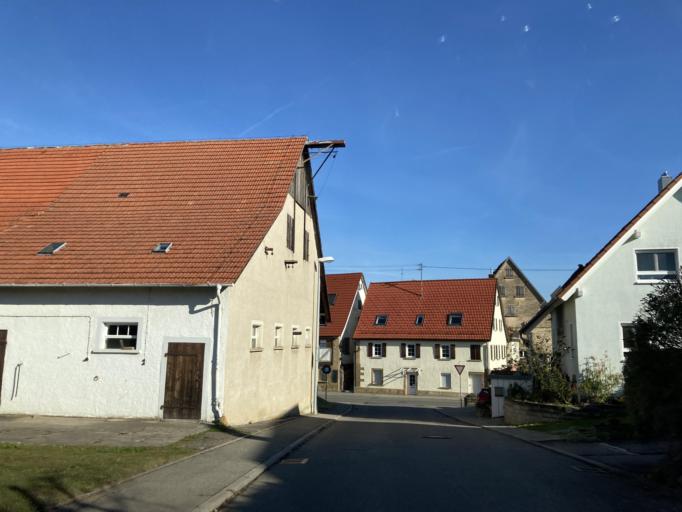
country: DE
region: Baden-Wuerttemberg
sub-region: Tuebingen Region
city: Rottenburg
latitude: 48.4802
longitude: 8.8816
